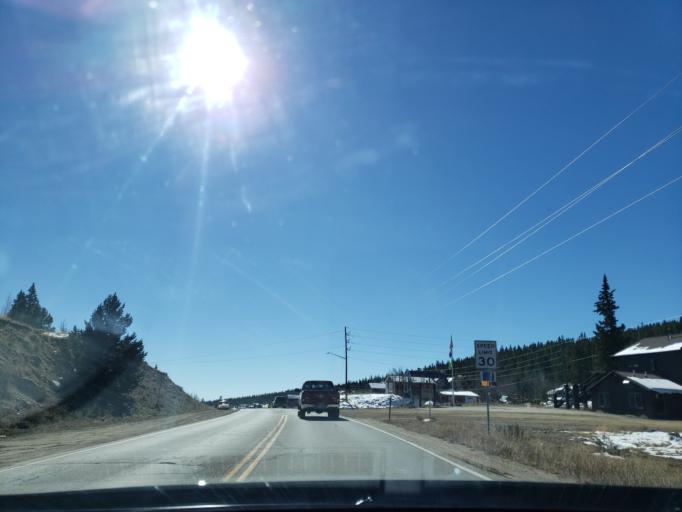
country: US
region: Colorado
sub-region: Park County
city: Fairplay
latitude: 39.2892
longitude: -106.0663
